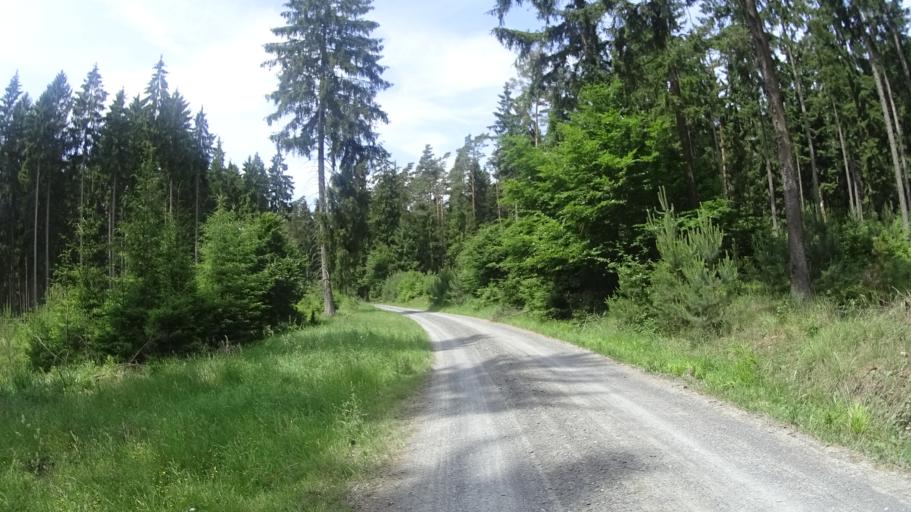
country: DE
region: Hesse
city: Rosenthal
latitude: 50.9496
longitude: 8.7987
